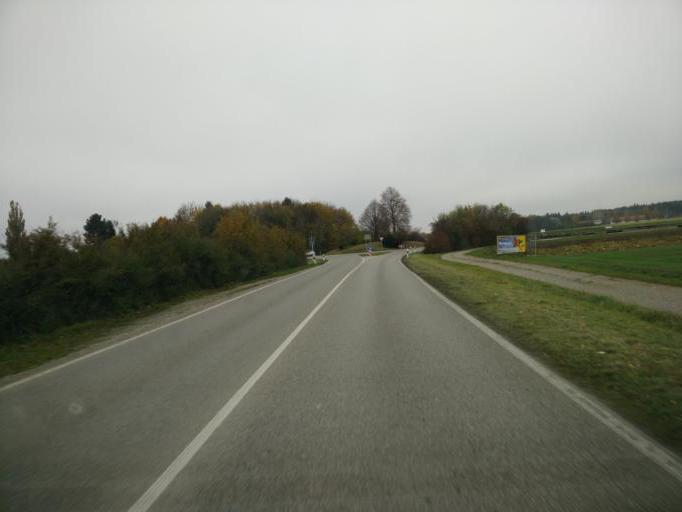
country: DE
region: Bavaria
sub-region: Swabia
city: Bad Worishofen
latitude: 48.0177
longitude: 10.6089
